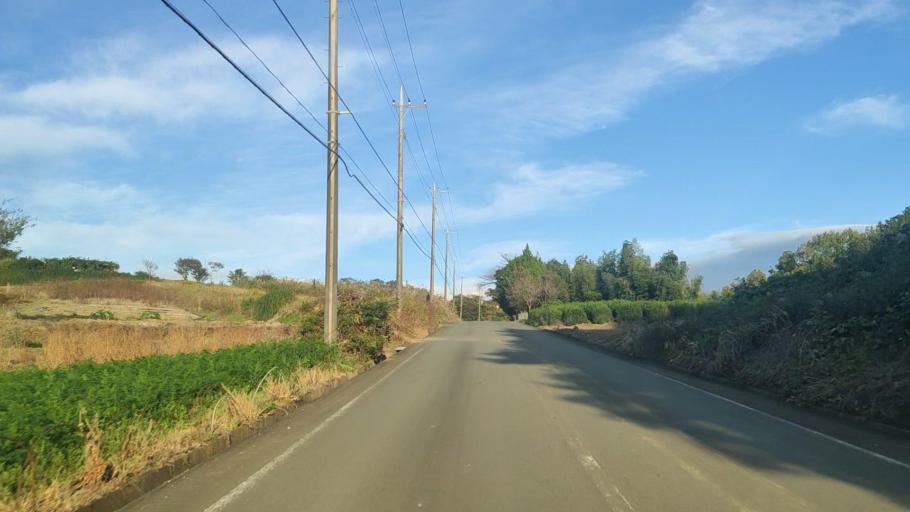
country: JP
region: Shizuoka
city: Mishima
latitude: 35.1431
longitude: 138.9542
